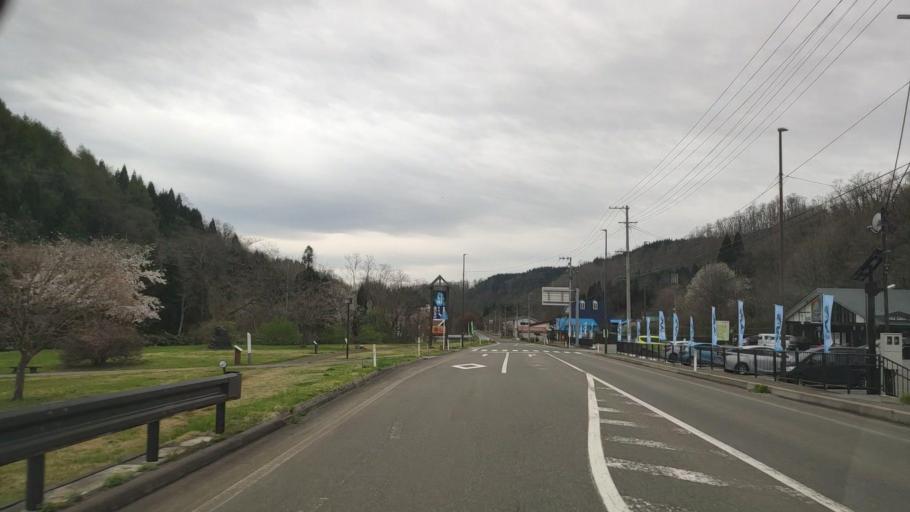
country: JP
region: Akita
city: Hanawa
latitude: 40.3571
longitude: 140.7831
